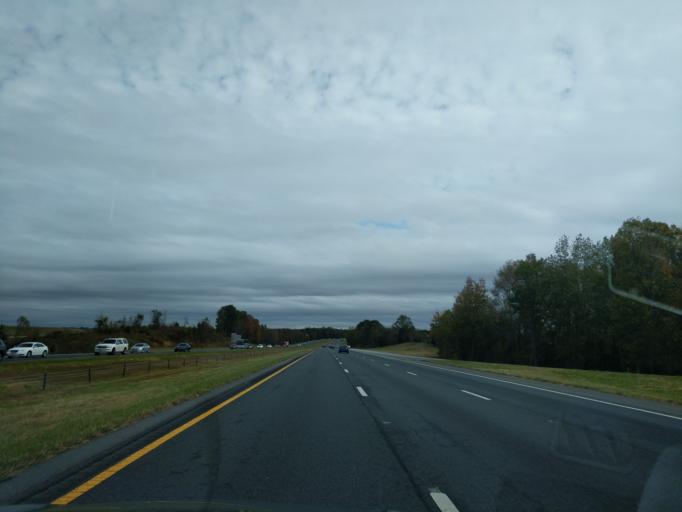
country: US
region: North Carolina
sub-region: Davidson County
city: Tyro
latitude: 35.7740
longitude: -80.3140
